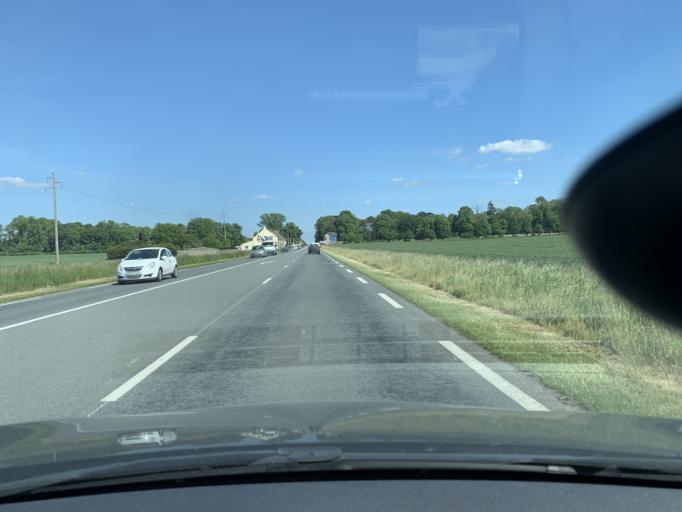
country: FR
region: Nord-Pas-de-Calais
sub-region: Departement du Nord
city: Fontaine-au-Pire
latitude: 50.1511
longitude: 3.3376
